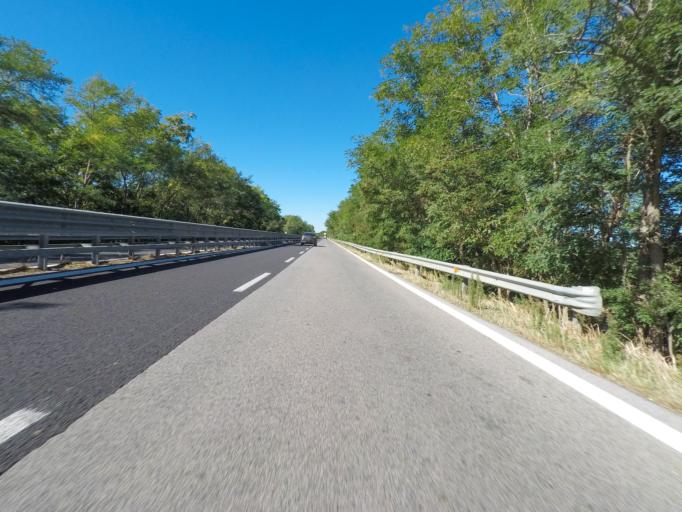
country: IT
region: Latium
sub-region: Provincia di Viterbo
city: Montalto di Castro
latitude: 42.2953
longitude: 11.6777
